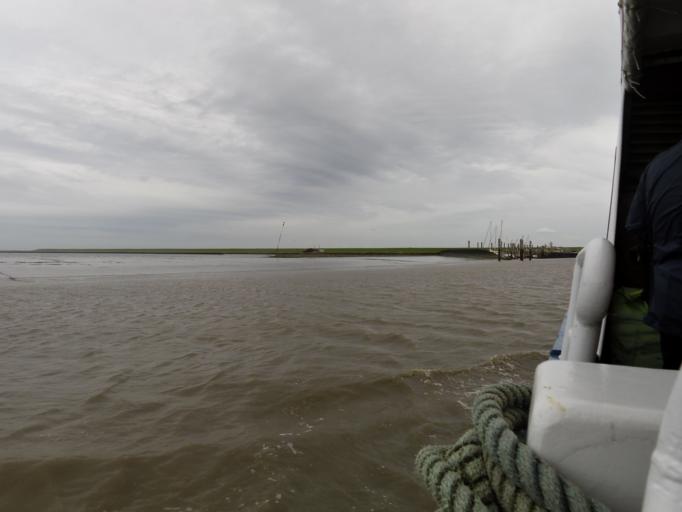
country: DE
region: Schleswig-Holstein
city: Grode
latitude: 54.6810
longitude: 8.7491
